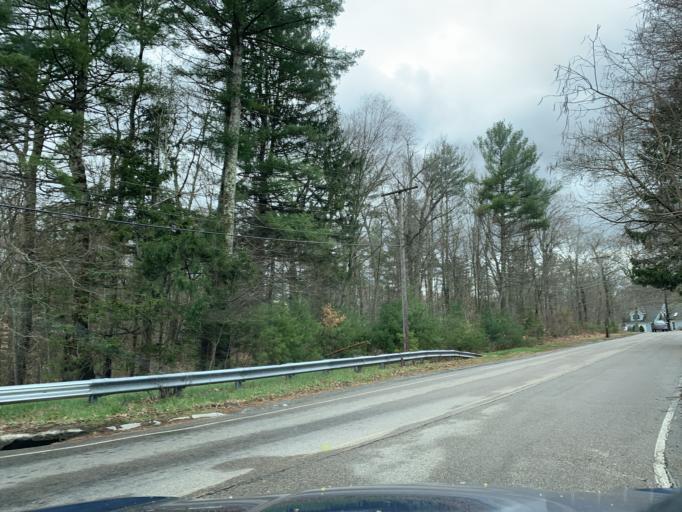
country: US
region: Massachusetts
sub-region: Bristol County
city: Norton
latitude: 41.9448
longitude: -71.2198
